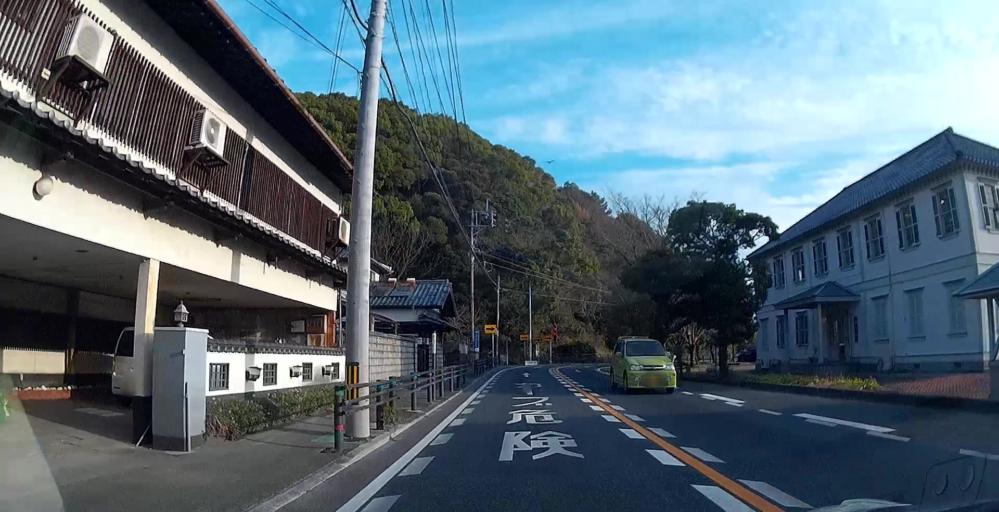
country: JP
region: Nagasaki
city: Shimabara
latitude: 32.6225
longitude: 130.4565
